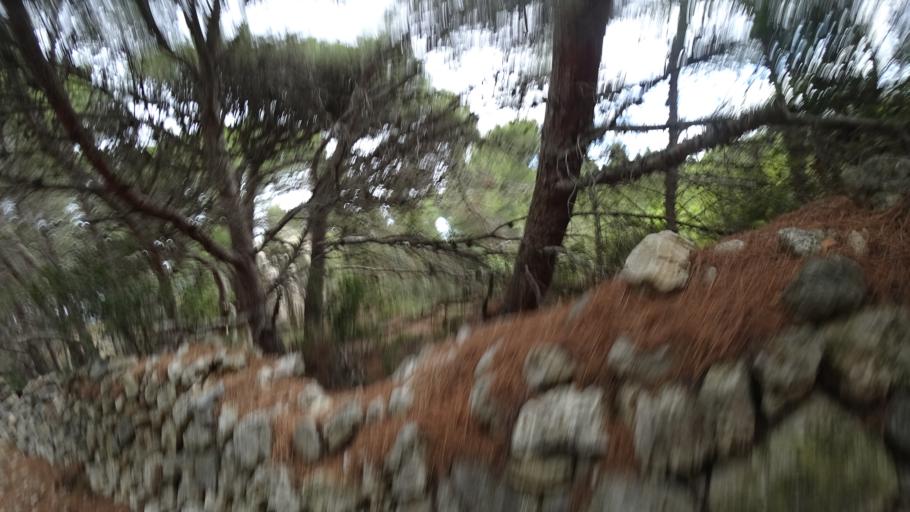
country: FR
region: Languedoc-Roussillon
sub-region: Departement de l'Aude
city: Leucate
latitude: 42.9076
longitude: 3.0264
